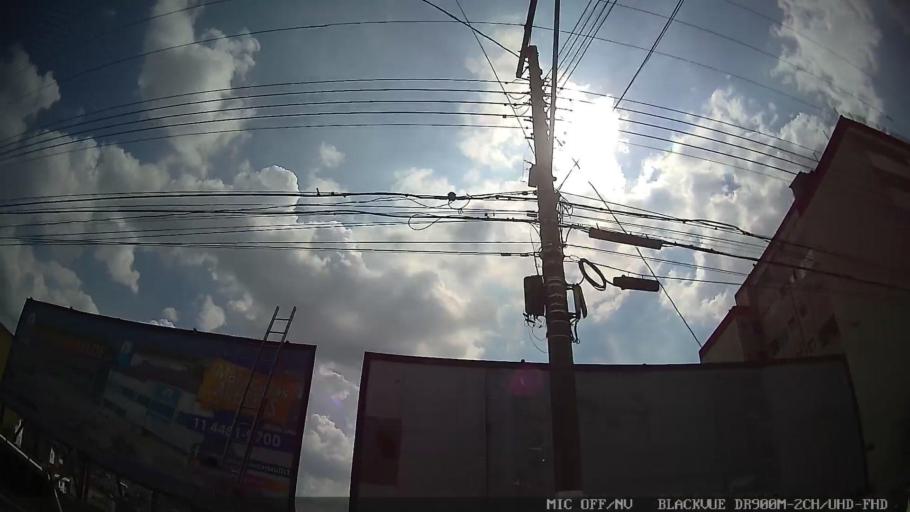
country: BR
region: Sao Paulo
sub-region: Braganca Paulista
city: Braganca Paulista
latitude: -22.9606
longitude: -46.5408
